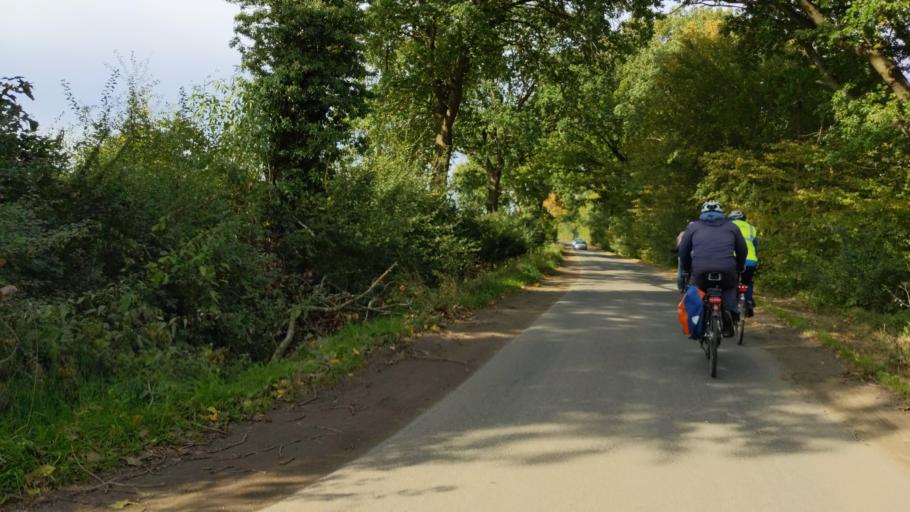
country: DE
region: Schleswig-Holstein
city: Zarpen
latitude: 53.8586
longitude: 10.5185
